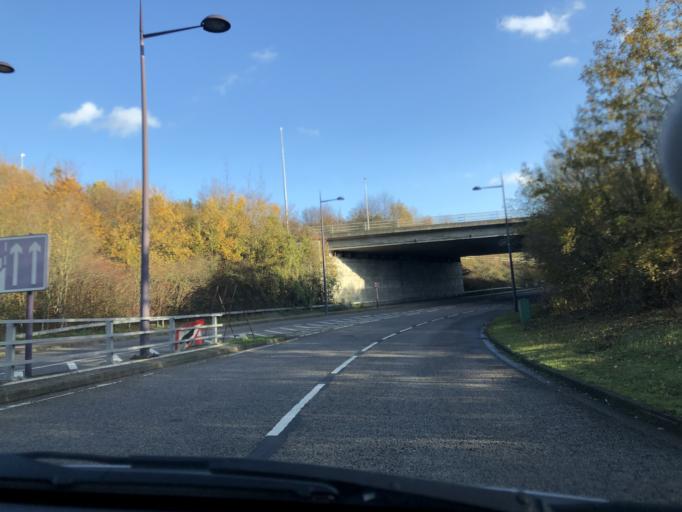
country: GB
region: England
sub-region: Kent
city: Greenhithe
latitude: 51.4413
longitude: 0.2790
